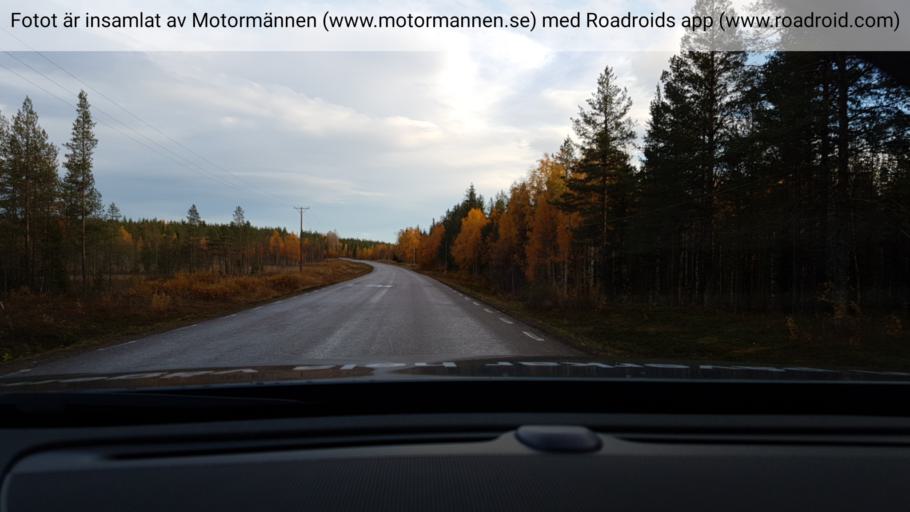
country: SE
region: Norrbotten
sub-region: Overkalix Kommun
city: OEverkalix
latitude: 67.0139
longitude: 22.5289
